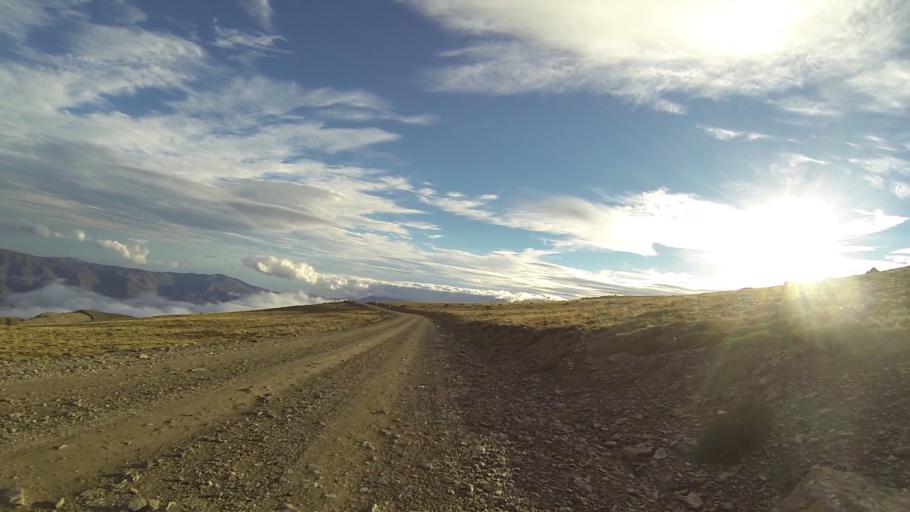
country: ES
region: Andalusia
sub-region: Provincia de Granada
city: Portugos
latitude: 36.9882
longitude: -3.3132
